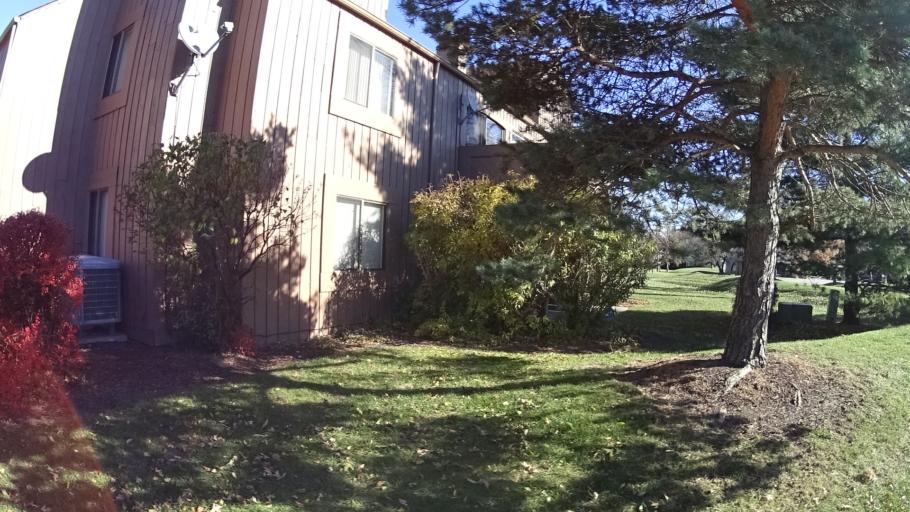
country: US
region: Ohio
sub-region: Lorain County
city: Avon Lake
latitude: 41.4943
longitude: -82.0165
